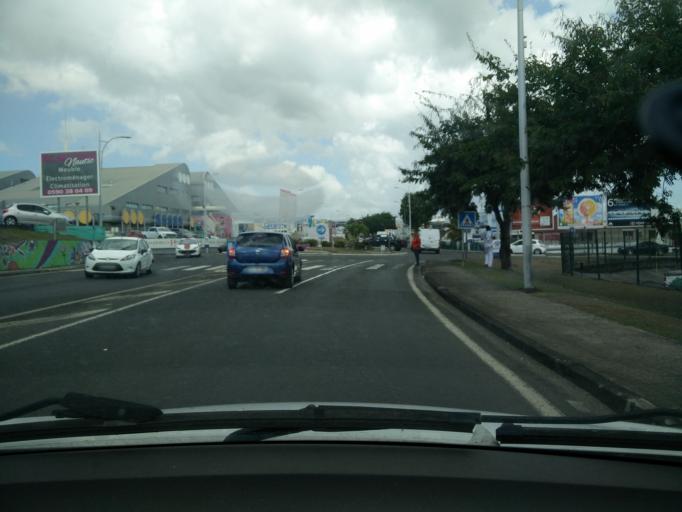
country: GP
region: Guadeloupe
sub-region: Guadeloupe
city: Pointe-a-Pitre
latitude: 16.2407
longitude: -61.5665
